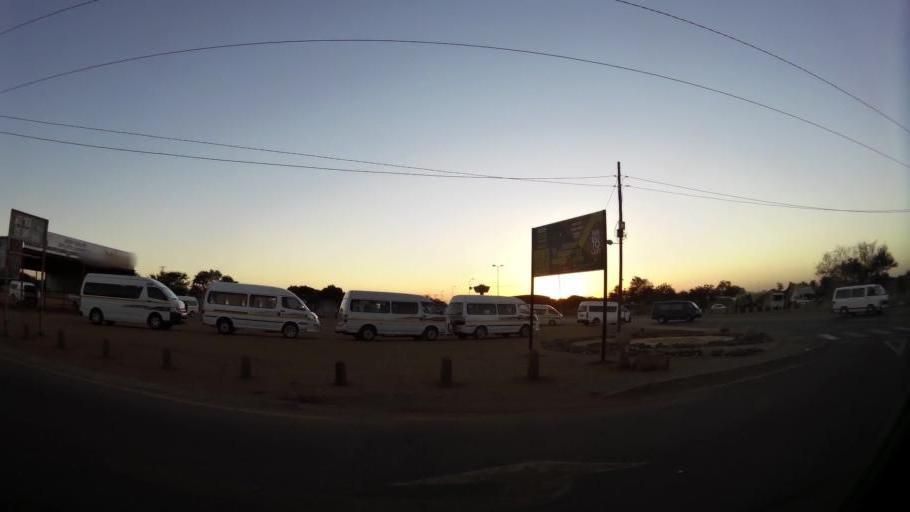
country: ZA
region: North-West
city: Ga-Rankuwa
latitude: -25.6192
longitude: 28.0069
